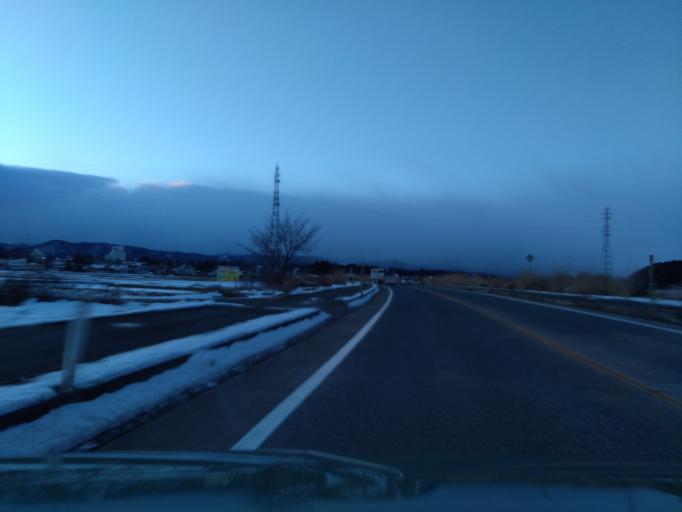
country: JP
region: Iwate
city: Shizukuishi
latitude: 39.7011
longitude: 140.9749
